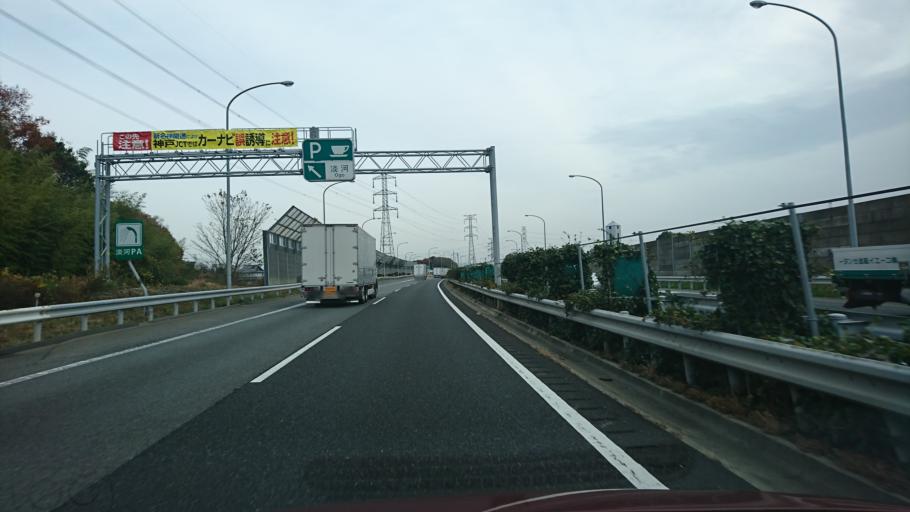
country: JP
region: Hyogo
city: Sandacho
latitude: 34.8287
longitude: 135.1507
